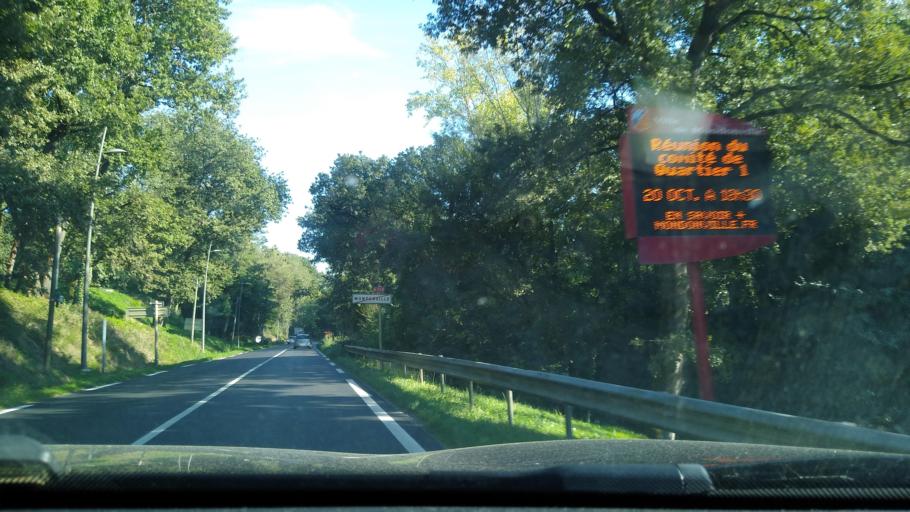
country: FR
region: Midi-Pyrenees
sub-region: Departement de la Haute-Garonne
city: Mondonville
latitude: 43.6725
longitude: 1.2883
